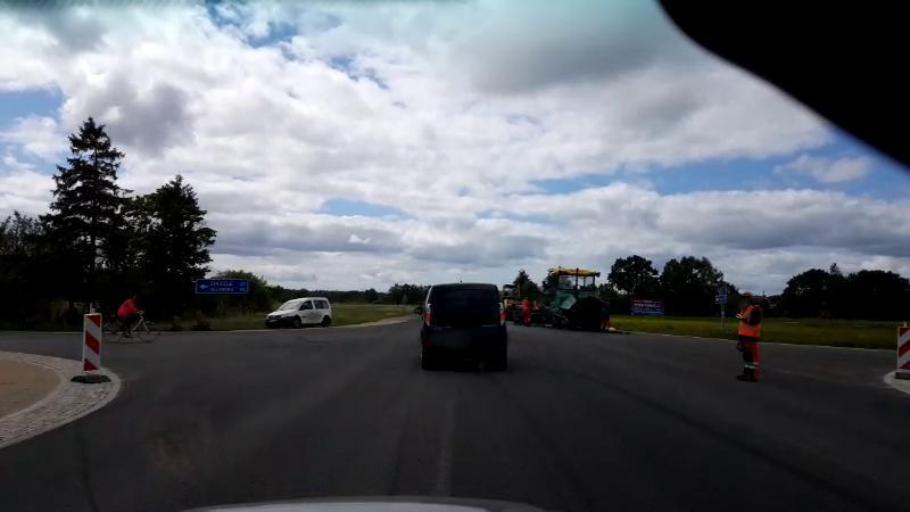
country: LV
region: Salacgrivas
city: Ainazi
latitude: 57.8602
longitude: 24.3679
